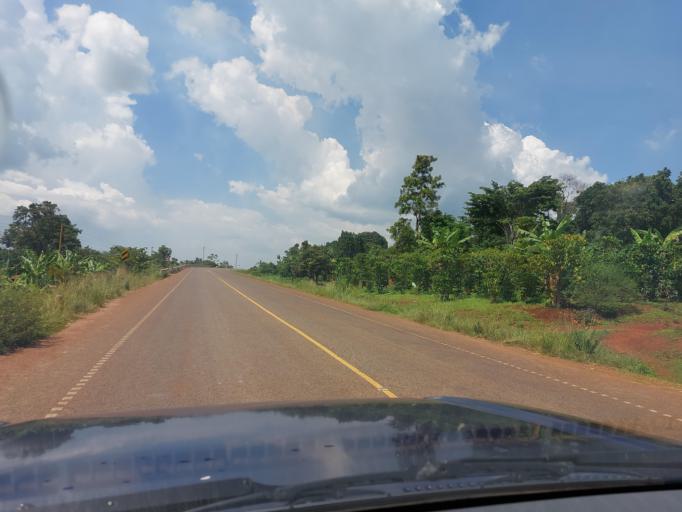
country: UG
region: Central Region
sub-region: Buikwe District
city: Buikwe
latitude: 0.2918
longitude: 33.0920
